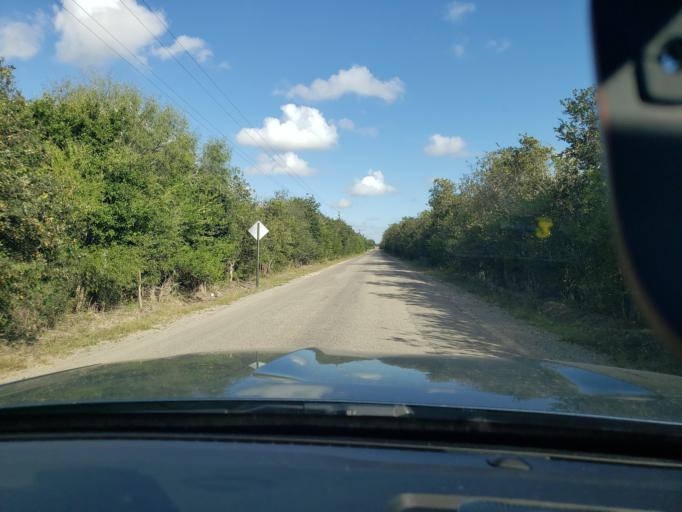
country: US
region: Texas
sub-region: Bee County
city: Beeville
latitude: 28.4488
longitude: -97.7170
